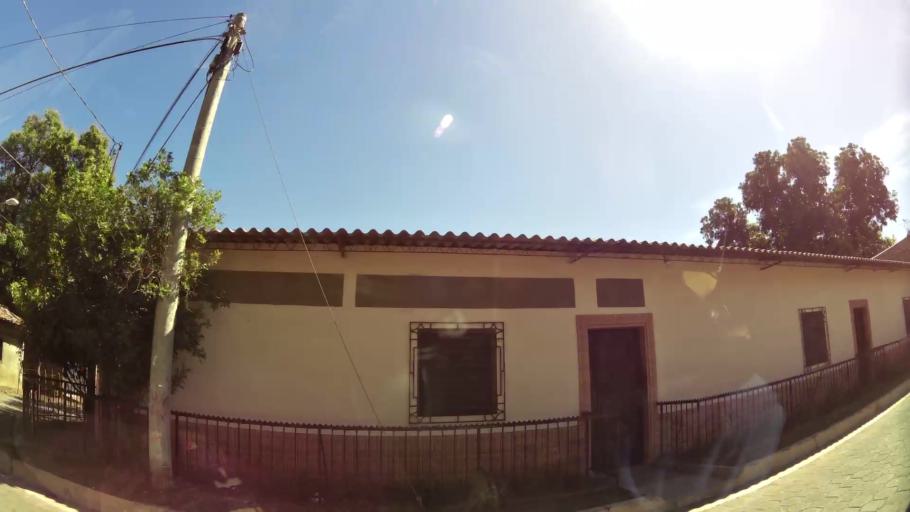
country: SV
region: San Miguel
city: San Miguel
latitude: 13.4940
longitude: -88.1711
